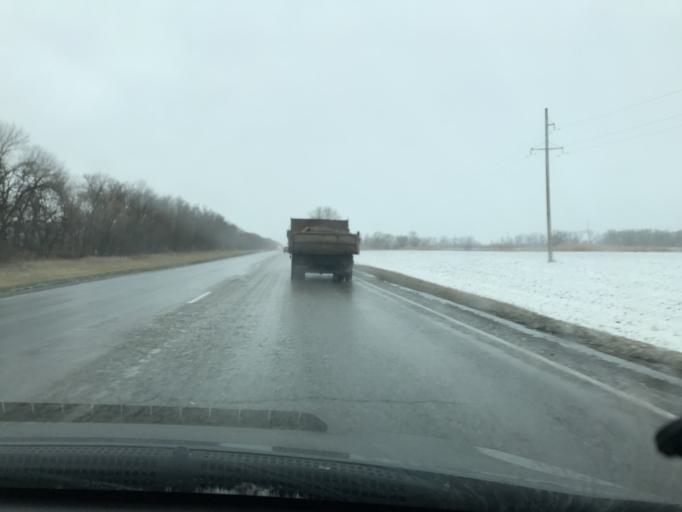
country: RU
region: Rostov
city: Zernograd
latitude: 46.8017
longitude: 40.3569
